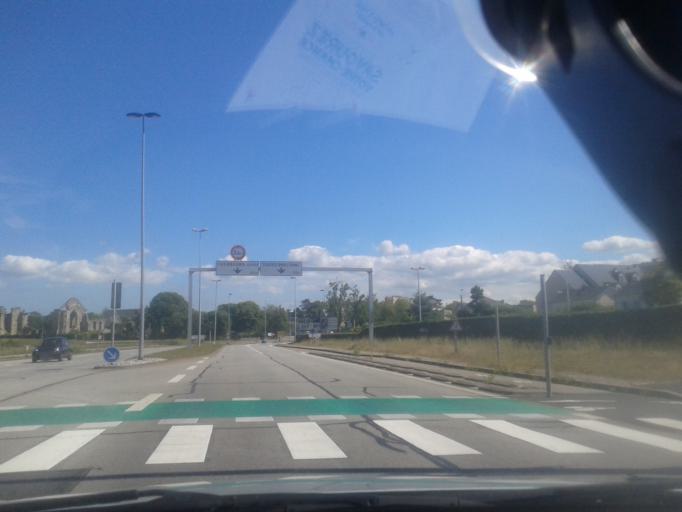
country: FR
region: Lower Normandy
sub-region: Departement de la Manche
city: Equeurdreville-Hainneville
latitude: 49.6489
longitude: -1.6442
